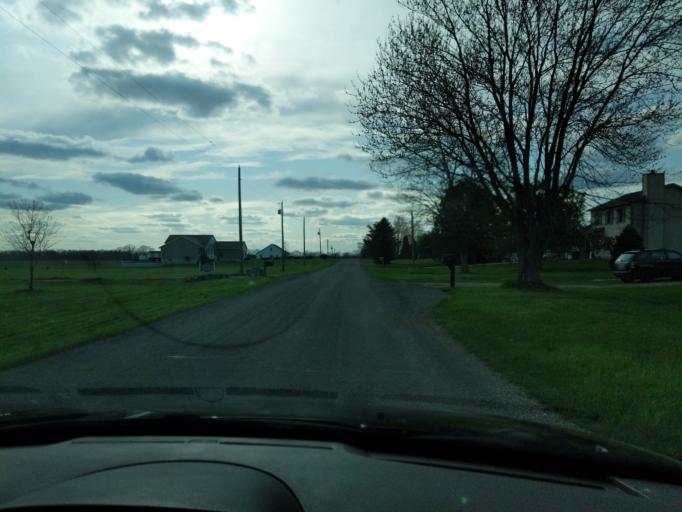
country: US
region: Ohio
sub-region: Champaign County
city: Urbana
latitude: 40.1362
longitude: -83.6825
